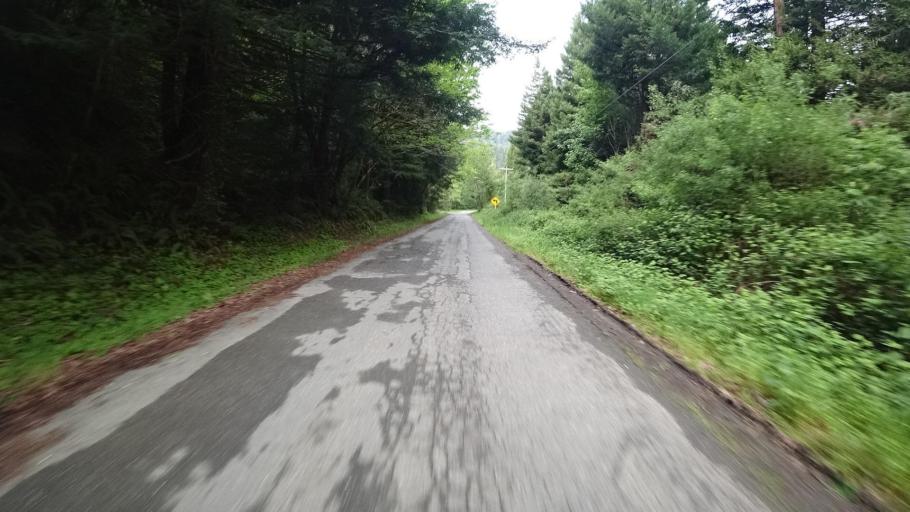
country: US
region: California
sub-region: Humboldt County
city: Redway
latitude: 40.3379
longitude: -123.9010
